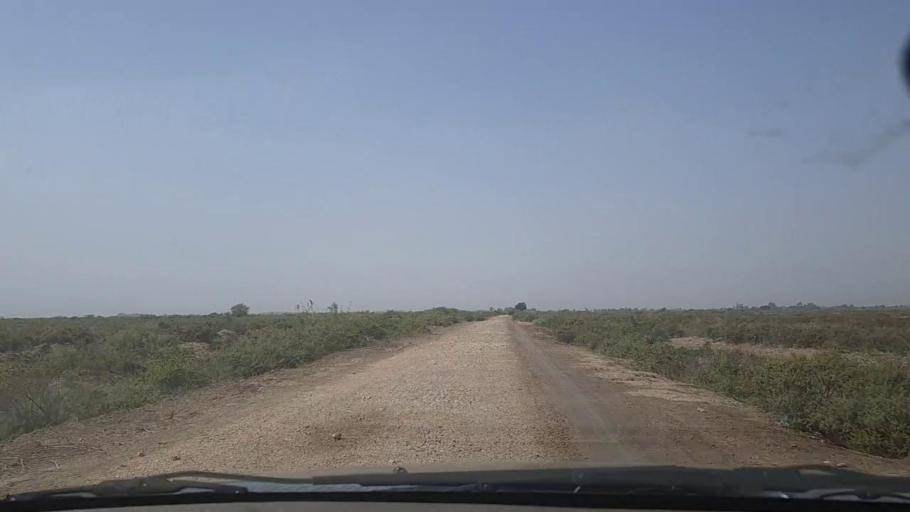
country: PK
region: Sindh
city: Keti Bandar
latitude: 24.2613
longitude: 67.6597
